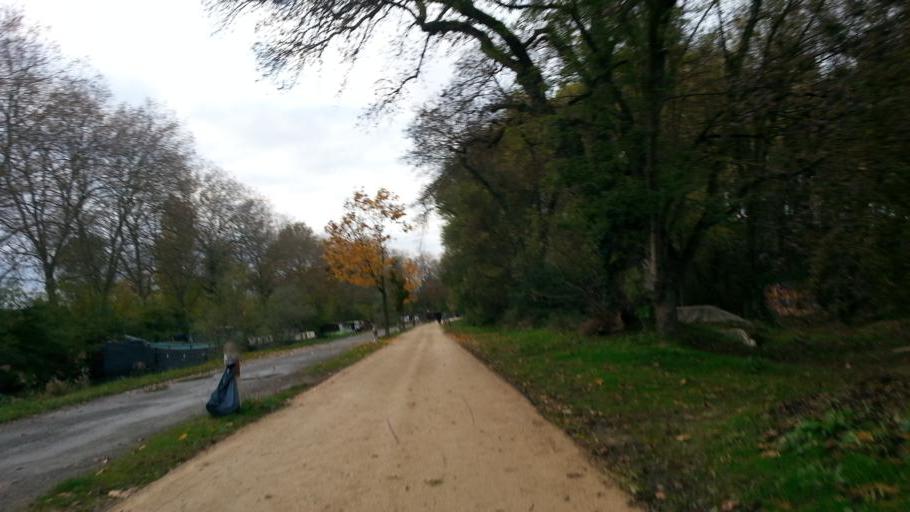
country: FR
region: Midi-Pyrenees
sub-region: Departement de la Haute-Garonne
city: Ramonville-Saint-Agne
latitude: 43.5454
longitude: 1.4882
